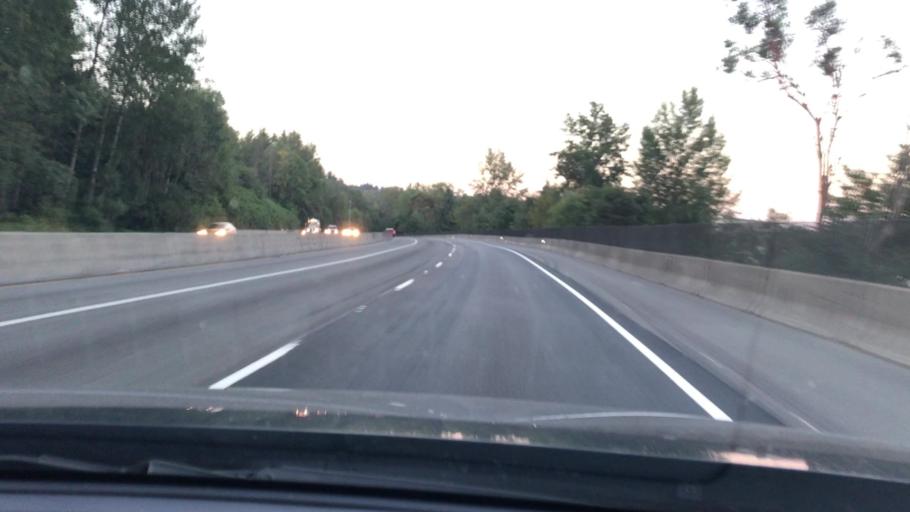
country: US
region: Washington
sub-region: King County
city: Newport
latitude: 47.5425
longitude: -122.1958
